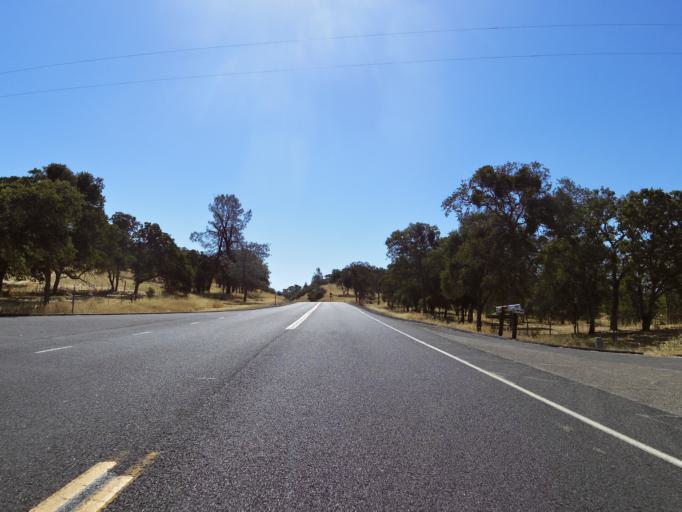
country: US
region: California
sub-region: Tuolumne County
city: Tuolumne City
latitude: 37.7001
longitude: -120.2897
